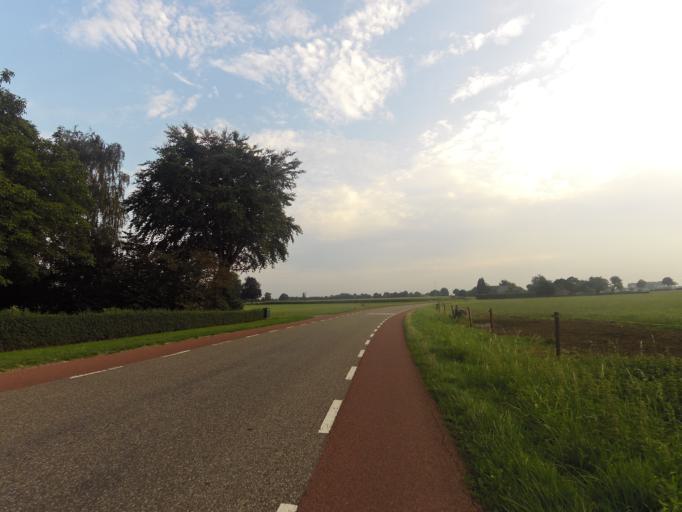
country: NL
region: Gelderland
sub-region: Oude IJsselstreek
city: Gendringen
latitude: 51.8559
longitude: 6.3908
